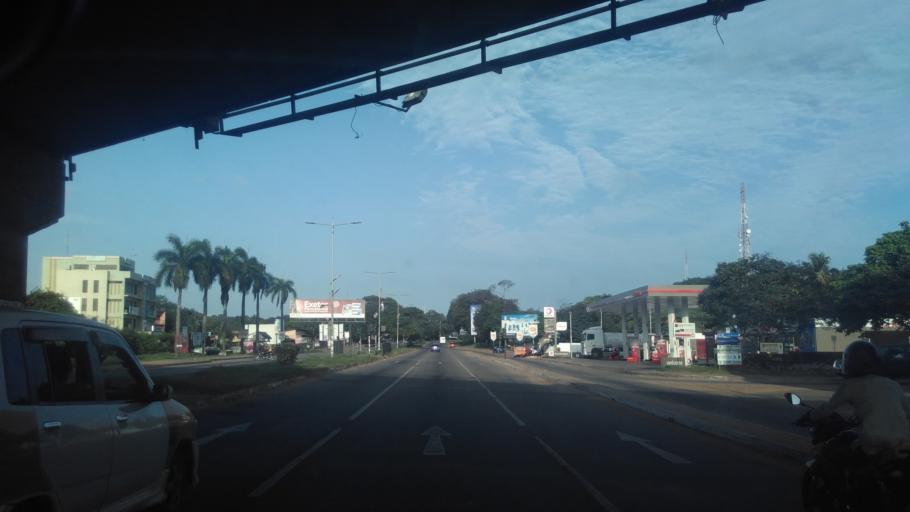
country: GH
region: Greater Accra
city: Accra
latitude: 5.5736
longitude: -0.1987
